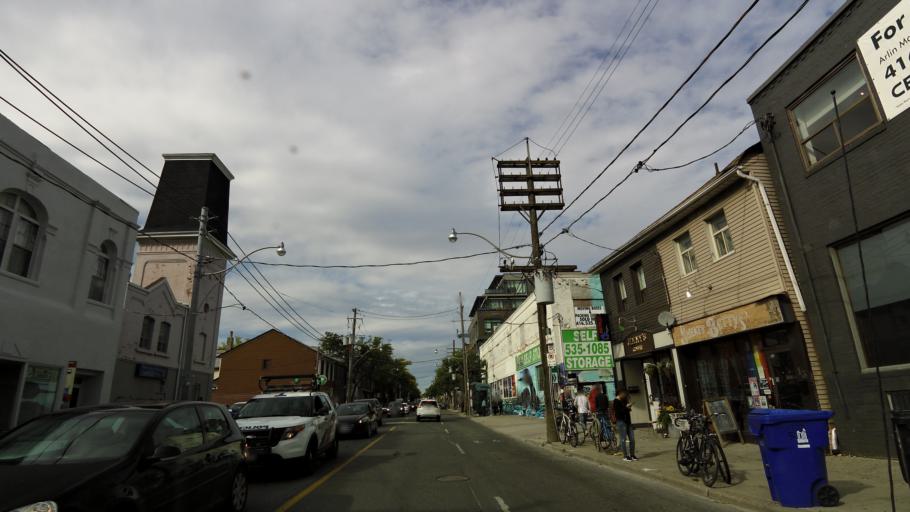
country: CA
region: Ontario
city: Toronto
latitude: 43.6443
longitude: -79.4189
